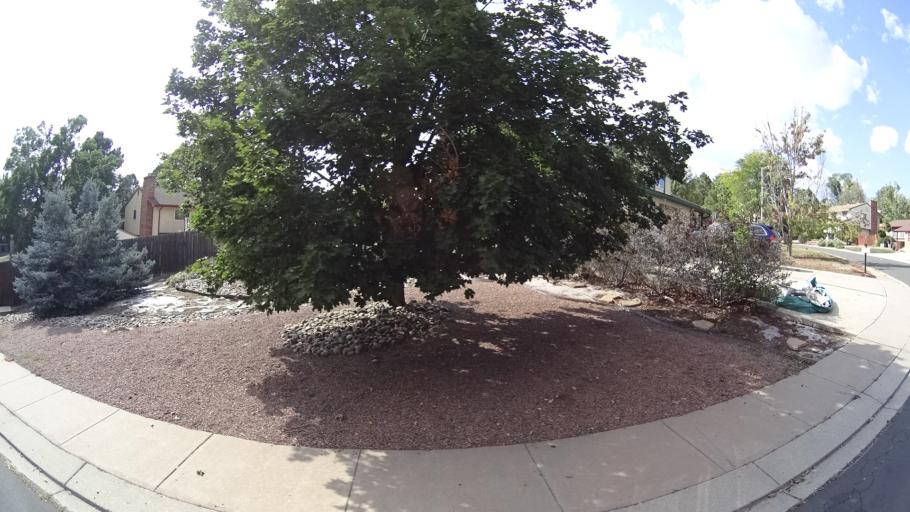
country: US
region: Colorado
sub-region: El Paso County
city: Cimarron Hills
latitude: 38.8693
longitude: -104.7270
